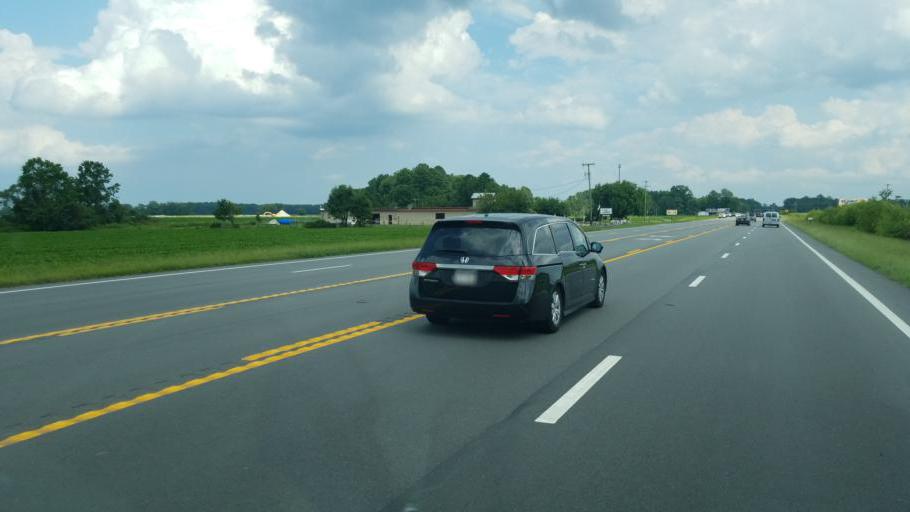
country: US
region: North Carolina
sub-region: Currituck County
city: Moyock
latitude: 36.5048
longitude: -76.1528
